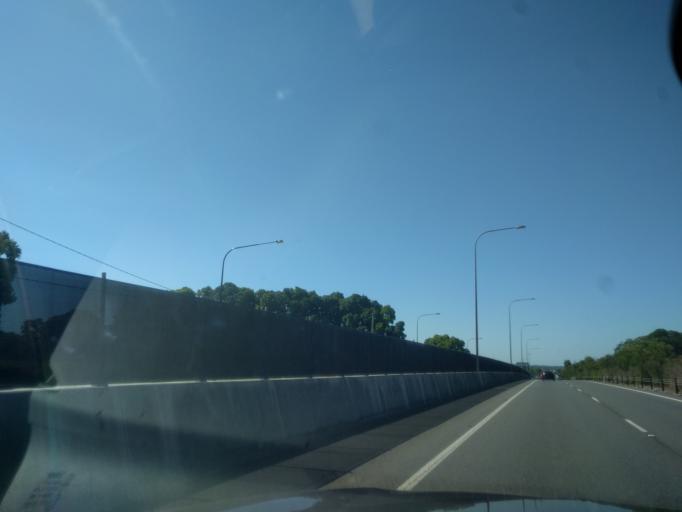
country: AU
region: Queensland
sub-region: Logan
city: Park Ridge South
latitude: -27.7051
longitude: 153.0381
